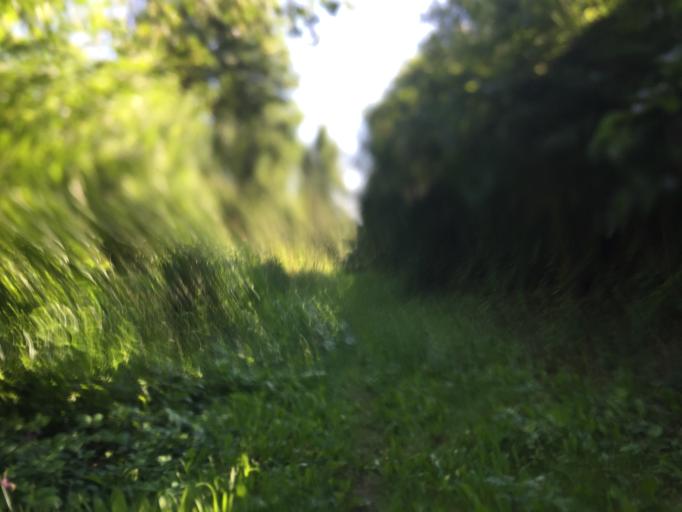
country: DE
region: Bavaria
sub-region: Regierungsbezirk Unterfranken
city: Goldbach
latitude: 49.9928
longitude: 9.1796
